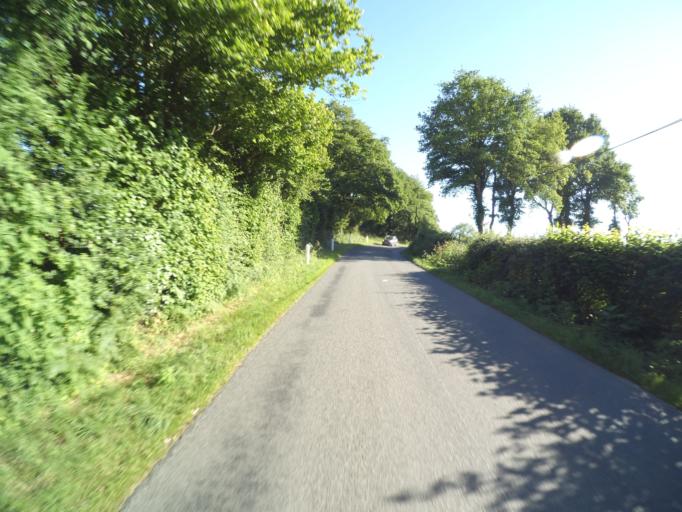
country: FR
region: Pays de la Loire
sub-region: Departement de la Vendee
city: La Flocelliere
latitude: 46.8138
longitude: -0.8538
